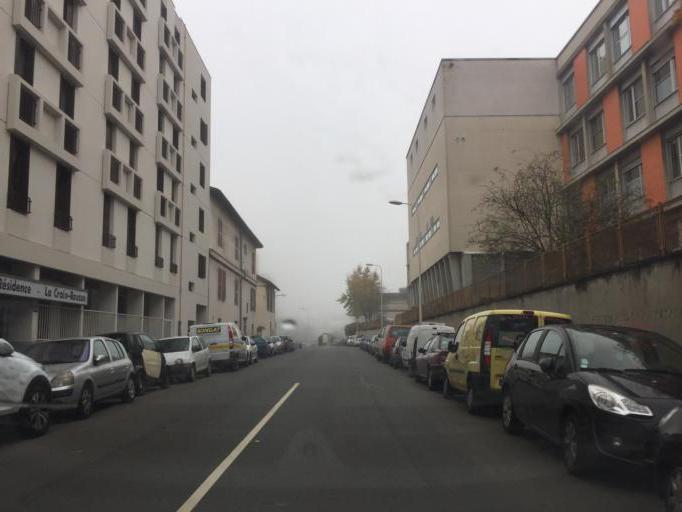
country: FR
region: Rhone-Alpes
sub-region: Departement du Rhone
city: Caluire-et-Cuire
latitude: 45.7802
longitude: 4.8292
